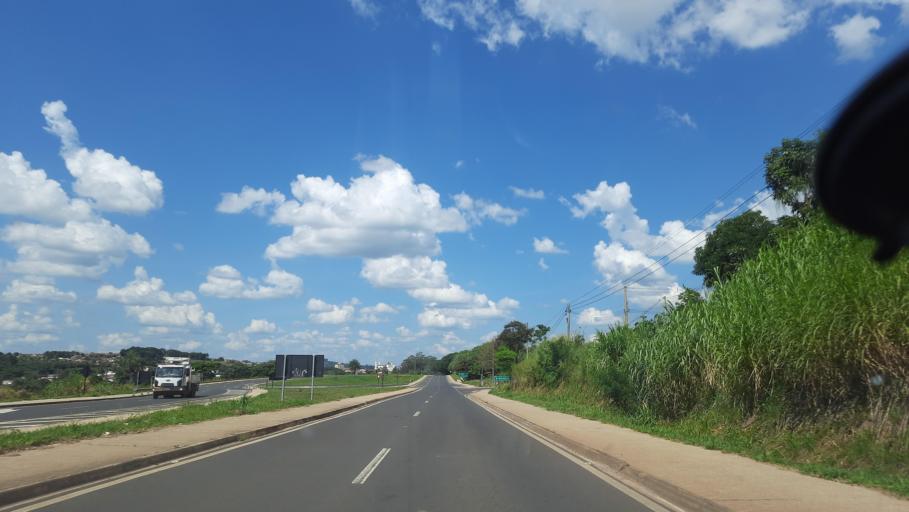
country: BR
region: Sao Paulo
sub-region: Sao Jose Do Rio Pardo
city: Sao Jose do Rio Pardo
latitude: -21.6027
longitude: -46.9122
